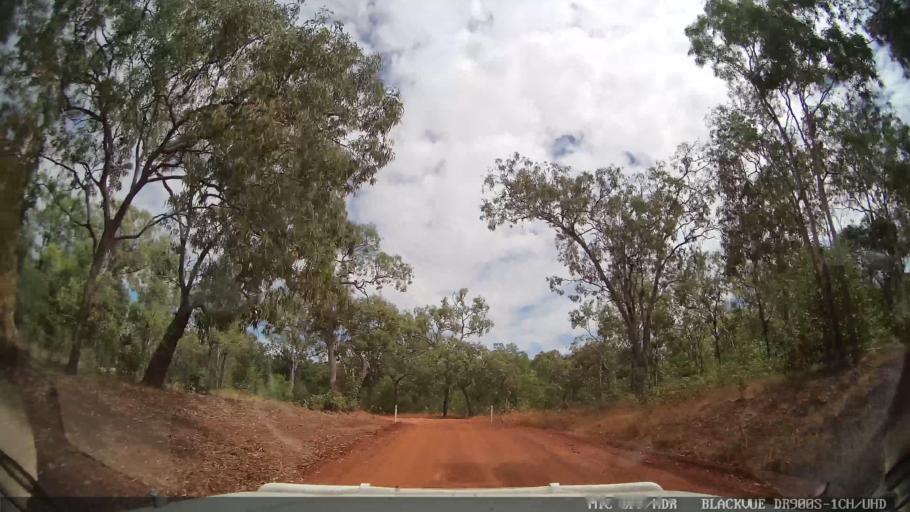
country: AU
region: Queensland
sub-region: Cook
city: Cooktown
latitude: -15.2927
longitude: 144.8431
